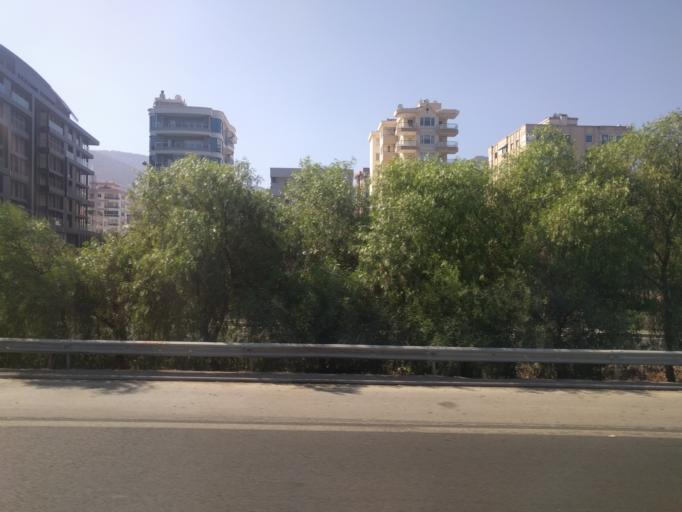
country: TR
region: Izmir
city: Karsiyaka
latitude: 38.3973
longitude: 27.0081
